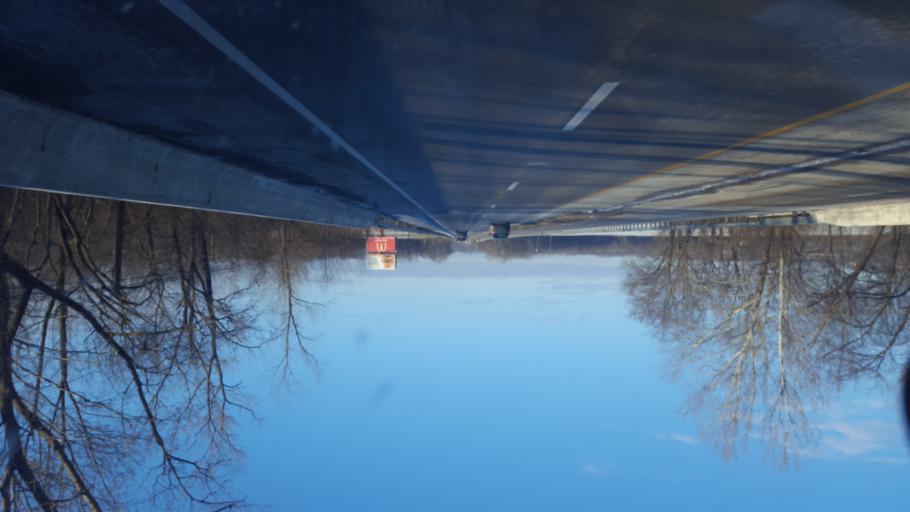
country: US
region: Ohio
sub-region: Pike County
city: Piketon
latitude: 39.0929
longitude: -83.0009
